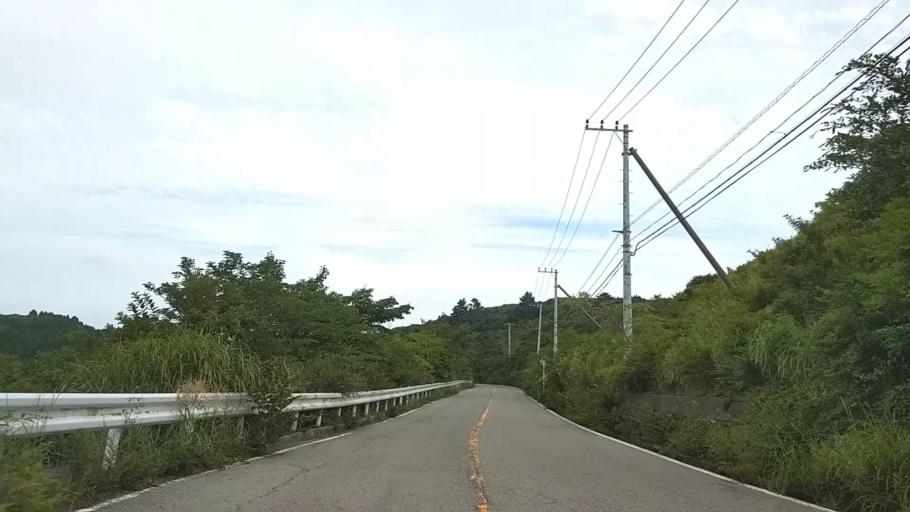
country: JP
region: Kanagawa
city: Hakone
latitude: 35.1826
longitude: 139.0578
